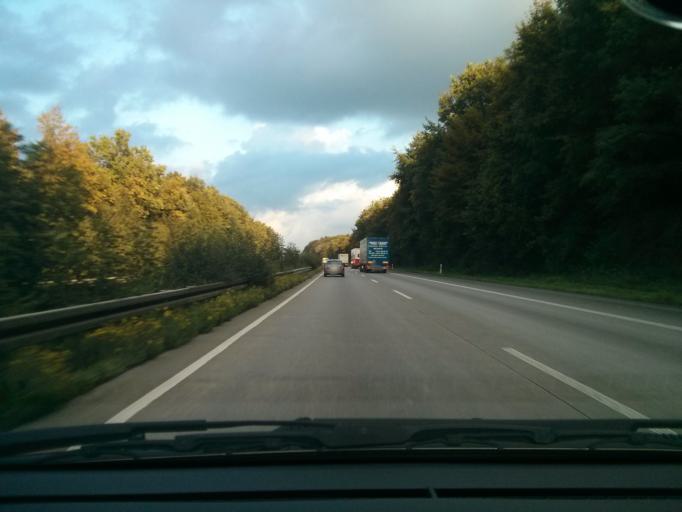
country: DE
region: North Rhine-Westphalia
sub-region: Regierungsbezirk Arnsberg
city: Frondenberg
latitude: 51.5244
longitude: 7.7796
